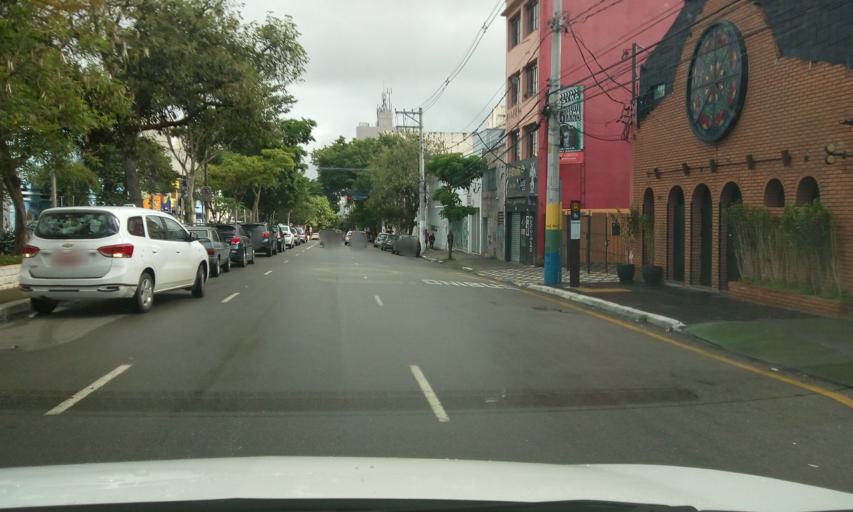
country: BR
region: Sao Paulo
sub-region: Sao Paulo
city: Sao Paulo
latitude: -23.5585
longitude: -46.6452
